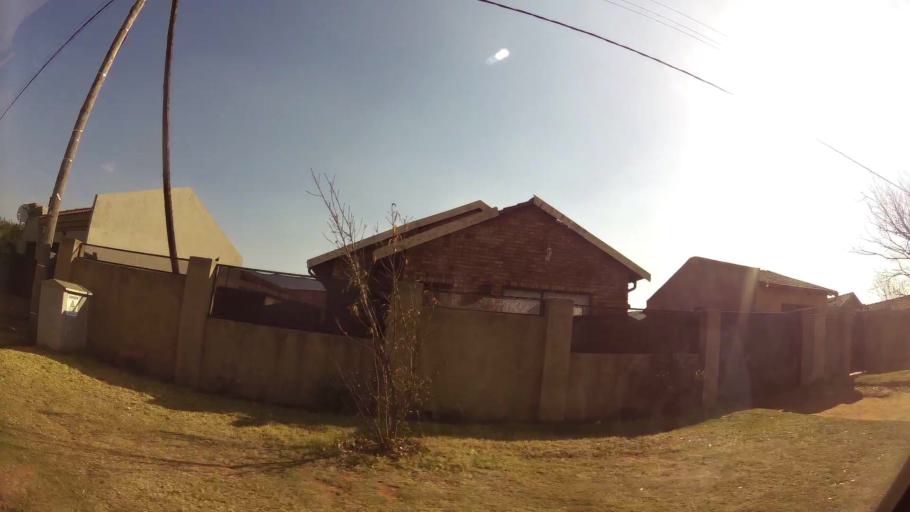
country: ZA
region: Gauteng
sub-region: Ekurhuleni Metropolitan Municipality
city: Benoni
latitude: -26.2252
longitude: 28.3280
